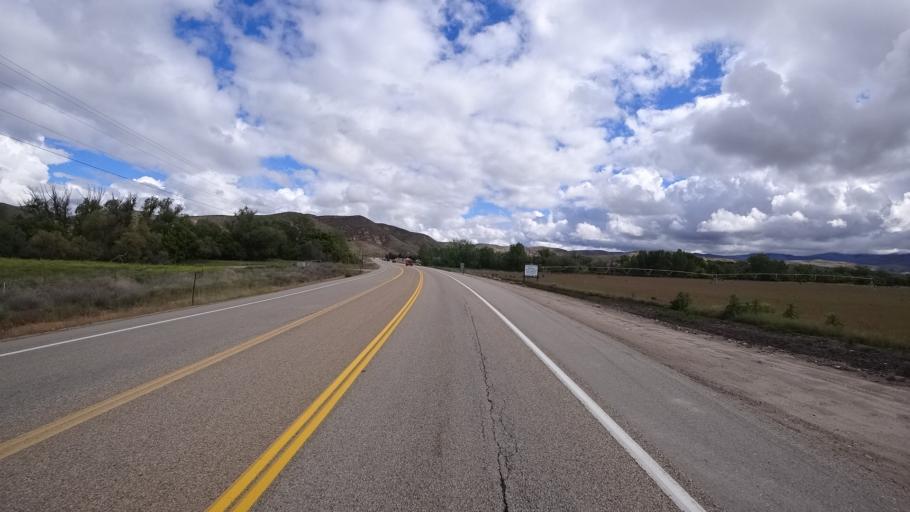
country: US
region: Idaho
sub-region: Ada County
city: Eagle
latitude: 43.7308
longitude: -116.3048
